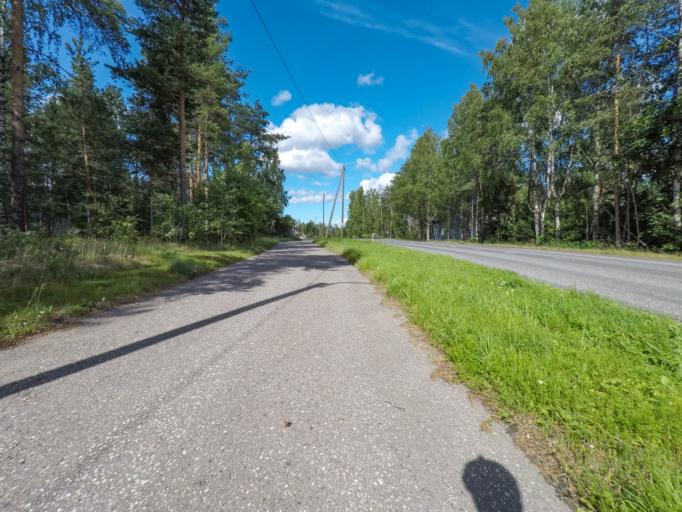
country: FI
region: South Karelia
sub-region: Lappeenranta
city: Lappeenranta
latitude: 61.0816
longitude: 28.3304
